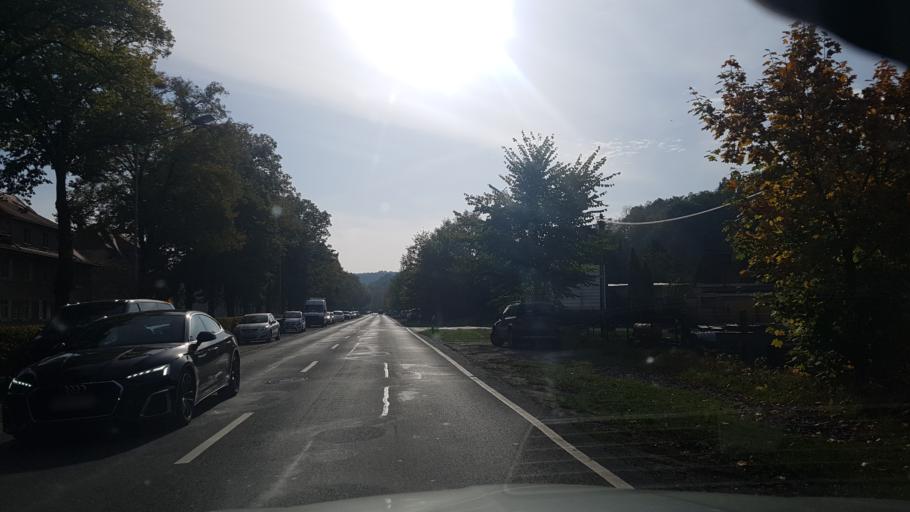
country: DE
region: Saxony
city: Dohma
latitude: 50.9362
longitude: 13.9463
